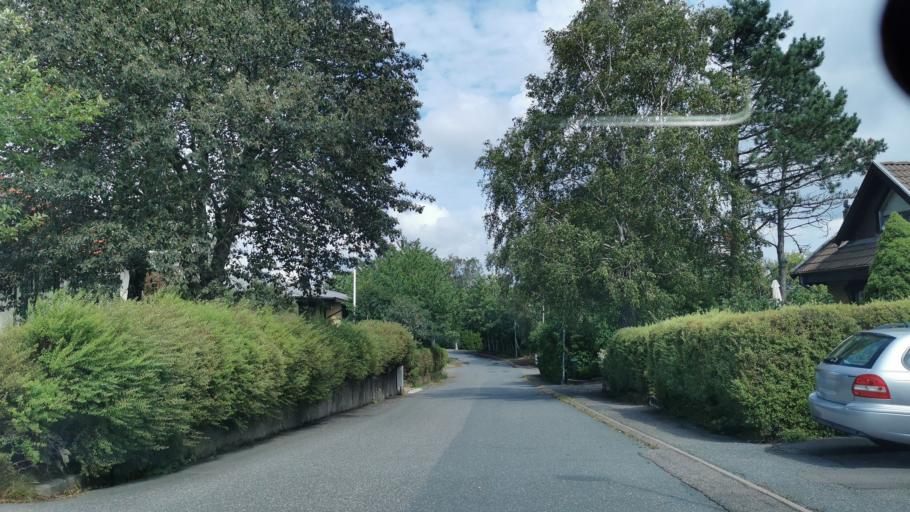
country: SE
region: Vaestra Goetaland
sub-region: Goteborg
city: Goeteborg
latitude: 57.6766
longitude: 11.9811
